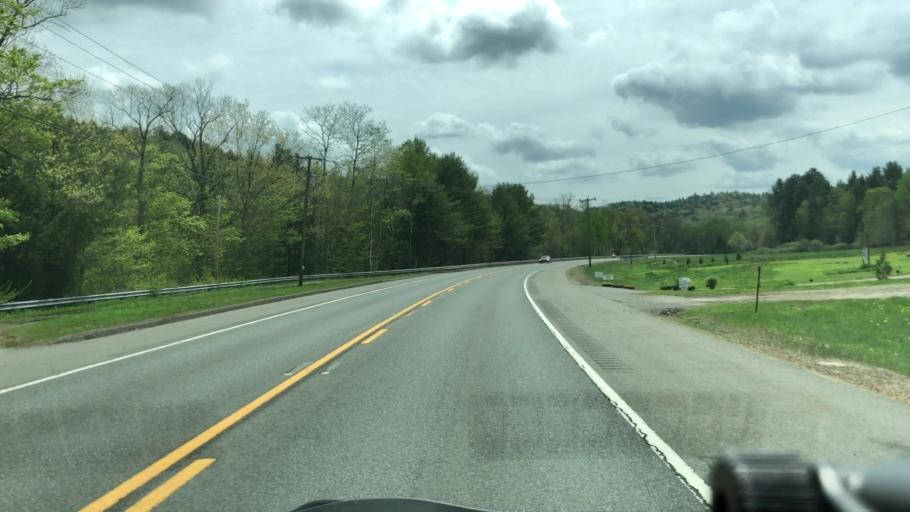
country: US
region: Massachusetts
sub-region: Hampshire County
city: Chesterfield
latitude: 42.4708
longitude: -72.9089
